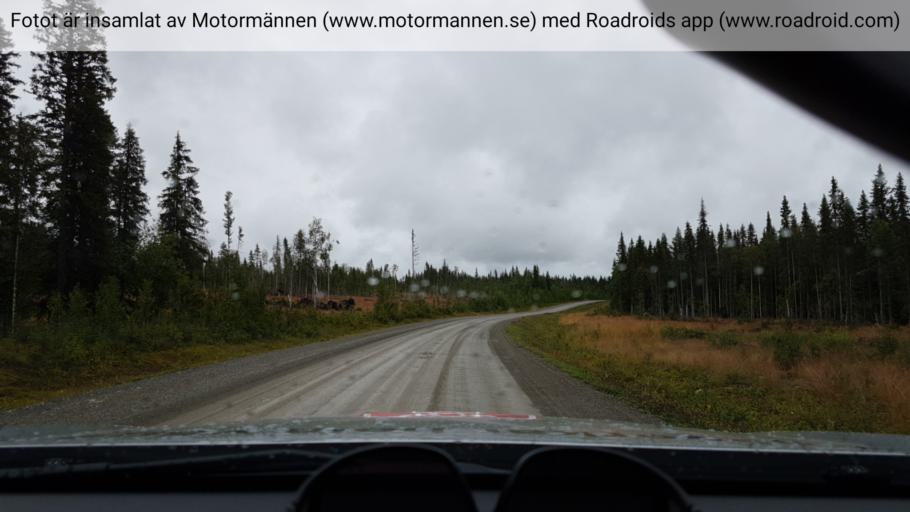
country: SE
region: Vaesterbotten
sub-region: Storumans Kommun
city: Storuman
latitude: 64.8714
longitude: 17.3476
